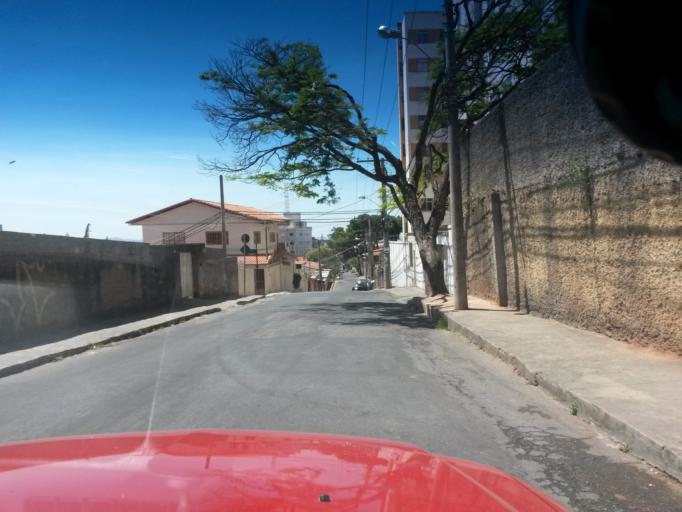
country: BR
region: Minas Gerais
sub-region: Belo Horizonte
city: Belo Horizonte
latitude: -19.9001
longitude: -43.9787
